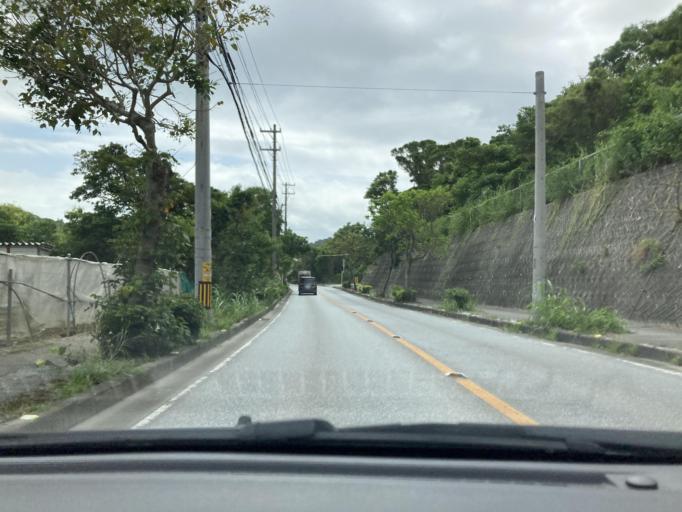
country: JP
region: Okinawa
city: Ginowan
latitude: 26.2754
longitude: 127.7810
